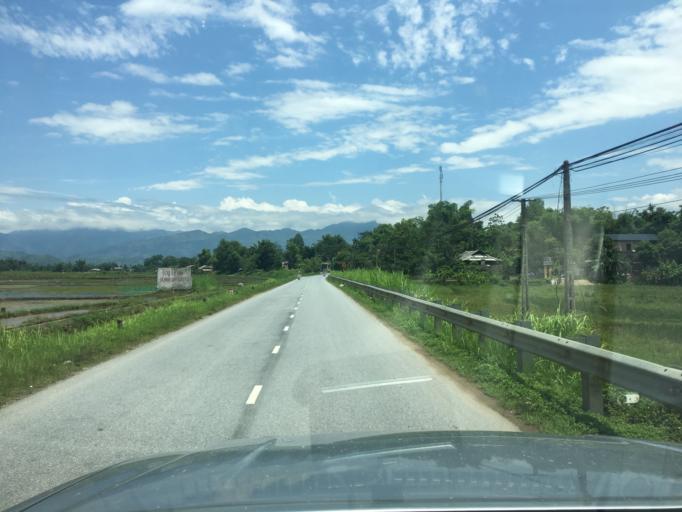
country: VN
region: Yen Bai
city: Son Thinh
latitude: 21.6336
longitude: 104.5042
